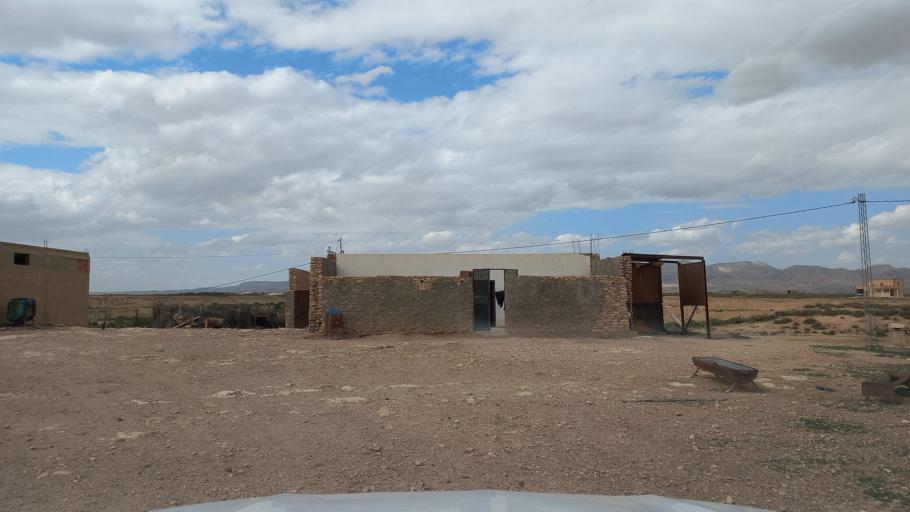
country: TN
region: Al Qasrayn
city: Sbiba
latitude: 35.3784
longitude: 9.0960
